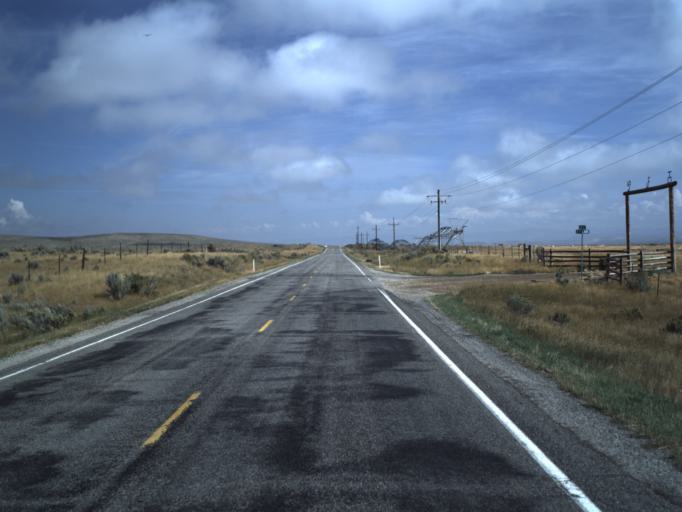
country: US
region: Utah
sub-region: Rich County
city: Randolph
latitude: 41.7486
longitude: -111.1463
